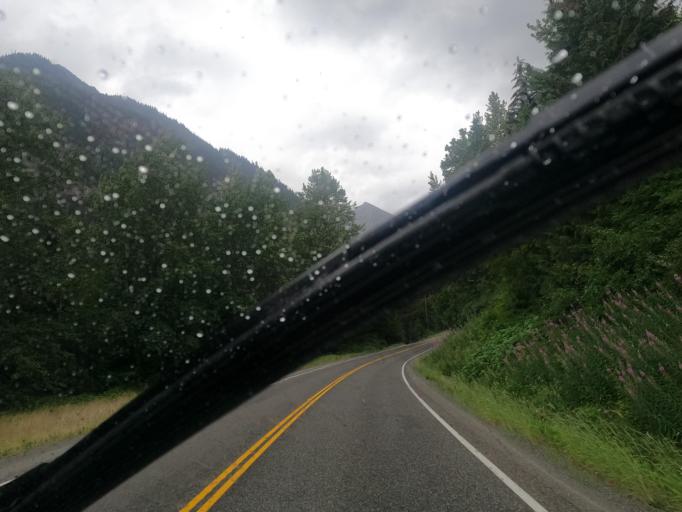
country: CA
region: British Columbia
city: Lillooet
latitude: 50.4799
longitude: -122.2155
